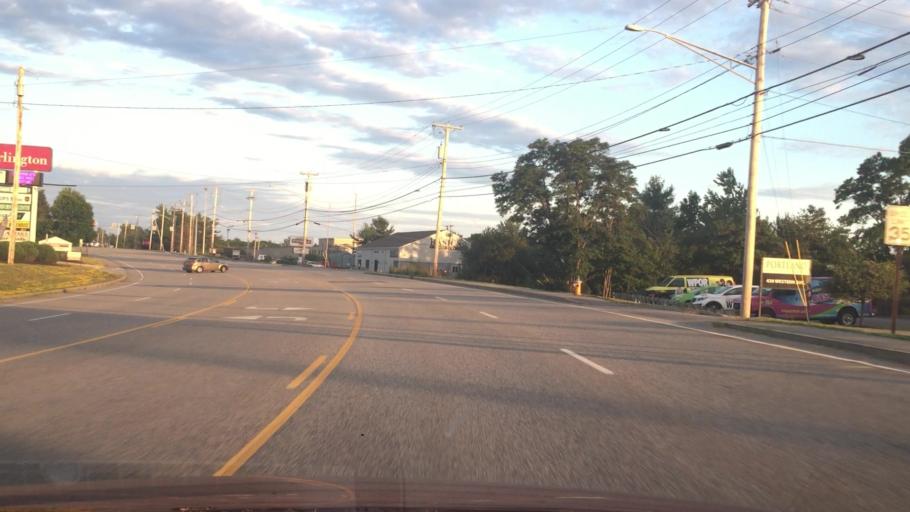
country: US
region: Maine
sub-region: Cumberland County
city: South Portland Gardens
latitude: 43.6428
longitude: -70.3295
